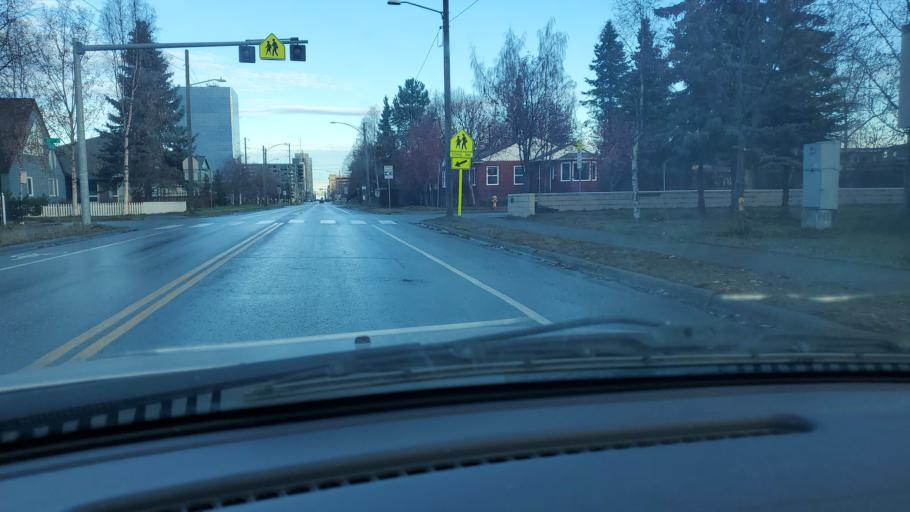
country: US
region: Alaska
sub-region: Anchorage Municipality
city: Anchorage
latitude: 61.2103
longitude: -149.8915
